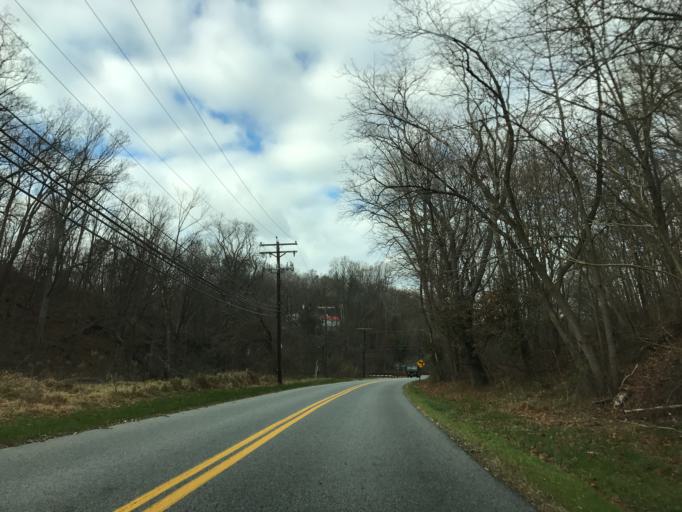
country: US
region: Maryland
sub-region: Baltimore County
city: Hunt Valley
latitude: 39.6254
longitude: -76.6332
